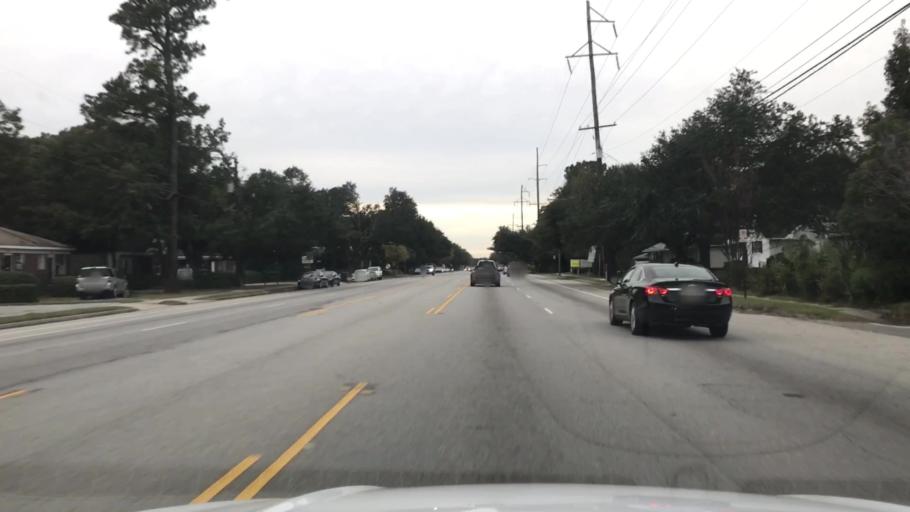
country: US
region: South Carolina
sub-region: Charleston County
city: Charleston
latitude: 32.7870
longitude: -79.9813
